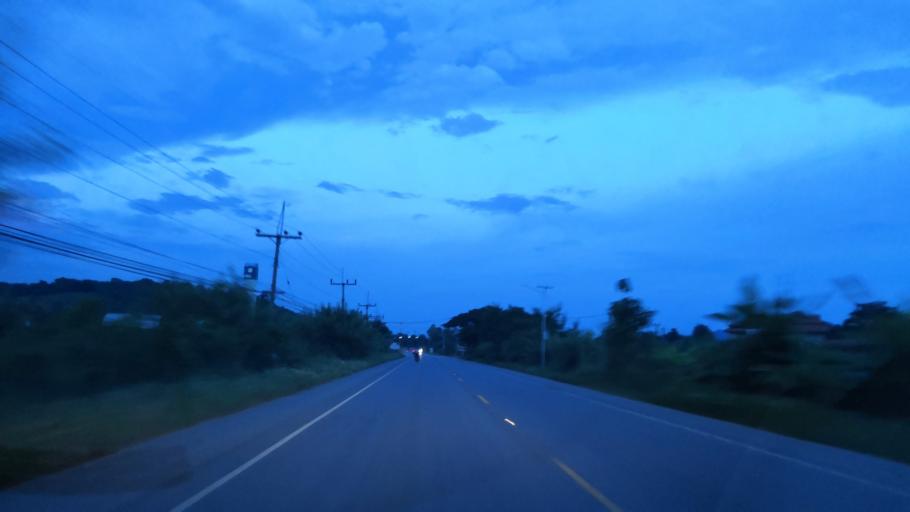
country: TH
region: Chiang Rai
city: Wiang Chiang Rung
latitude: 19.9921
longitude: 100.0333
